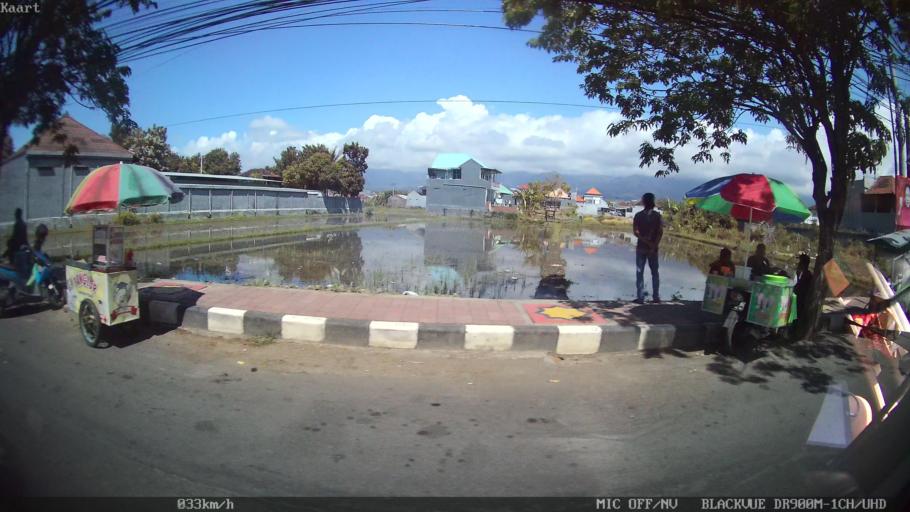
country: ID
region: Bali
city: Banjar Galiran
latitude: -8.1205
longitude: 115.0725
